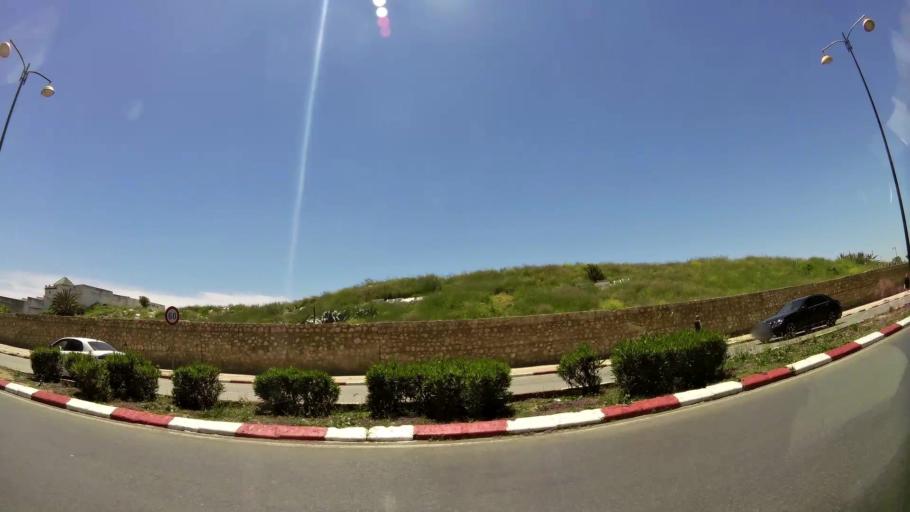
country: MA
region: Meknes-Tafilalet
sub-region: Meknes
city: Meknes
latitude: 33.9034
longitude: -5.5708
